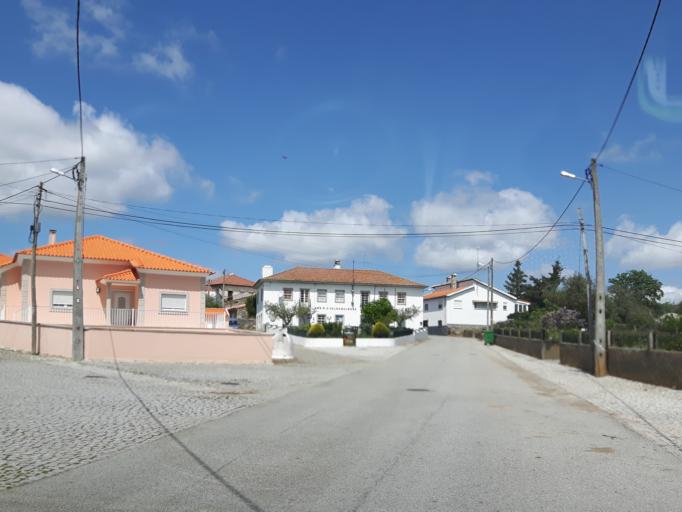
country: ES
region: Castille and Leon
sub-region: Provincia de Salamanca
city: Aldea del Obispo
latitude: 40.7034
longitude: -6.8182
